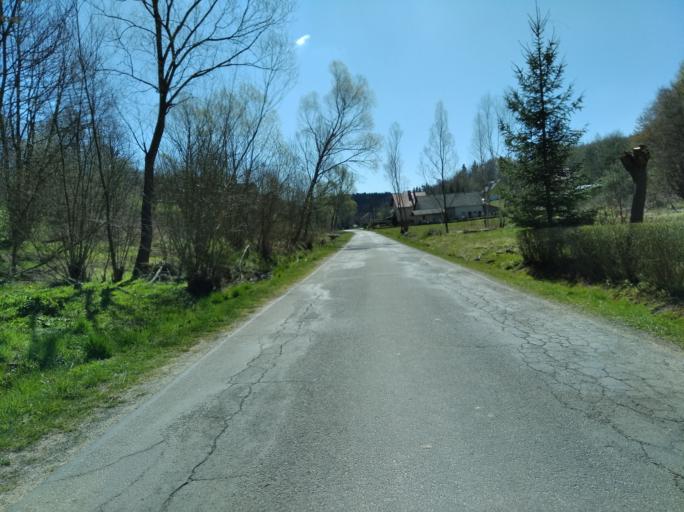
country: PL
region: Subcarpathian Voivodeship
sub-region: Powiat brzozowski
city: Jablonka
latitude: 49.7326
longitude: 22.1468
